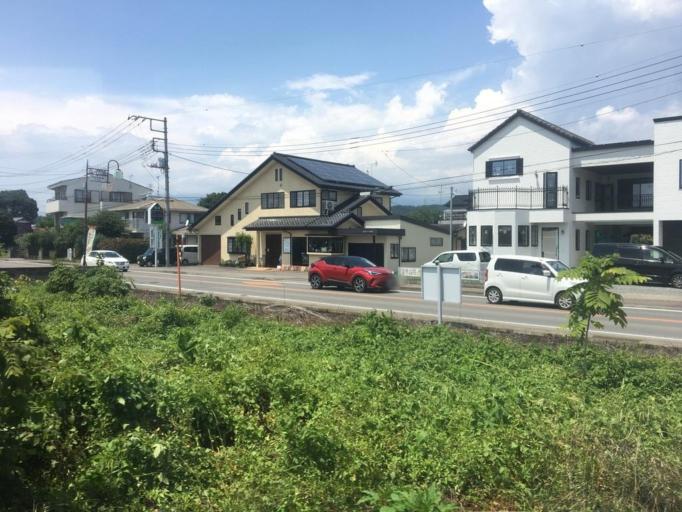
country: JP
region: Gunma
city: Omamacho-omama
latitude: 36.4188
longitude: 139.2613
